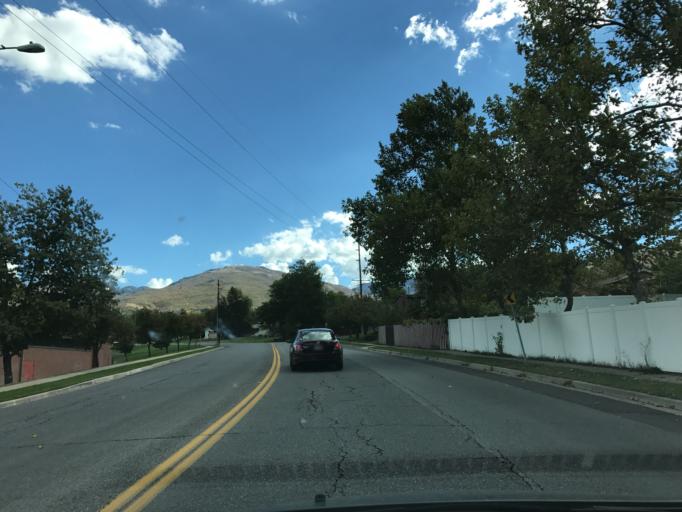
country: US
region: Utah
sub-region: Davis County
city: Woods Cross
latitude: 40.8707
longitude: -111.8750
